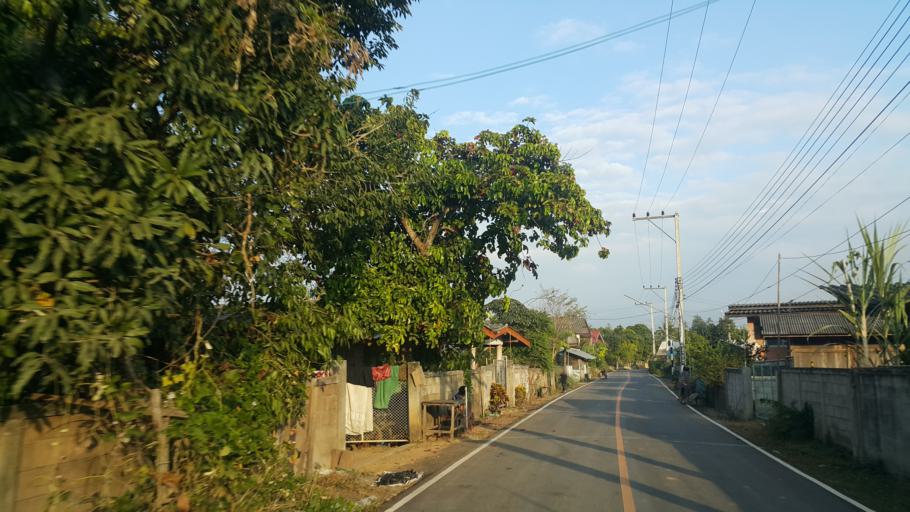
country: TH
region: Lampang
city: Sop Prap
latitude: 17.9433
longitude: 99.3410
